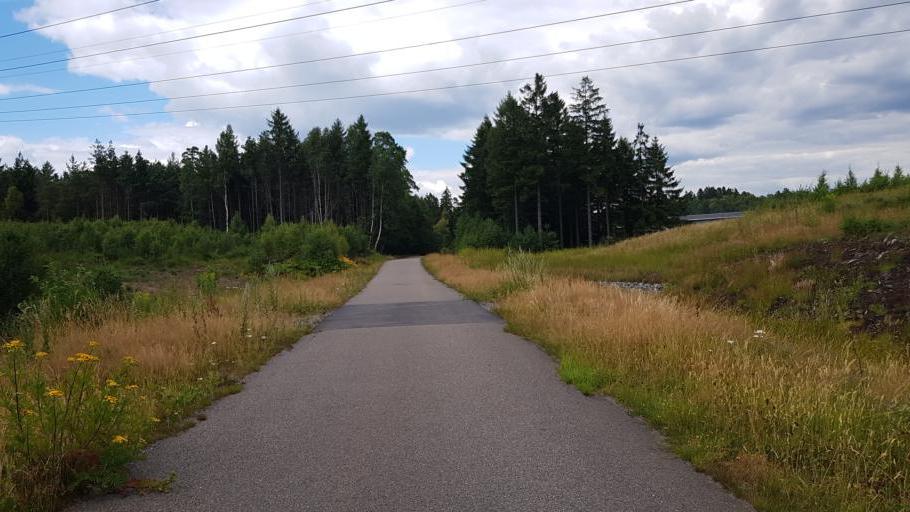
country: SE
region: Vaestra Goetaland
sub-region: Partille Kommun
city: Ojersjo
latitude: 57.6786
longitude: 12.0865
